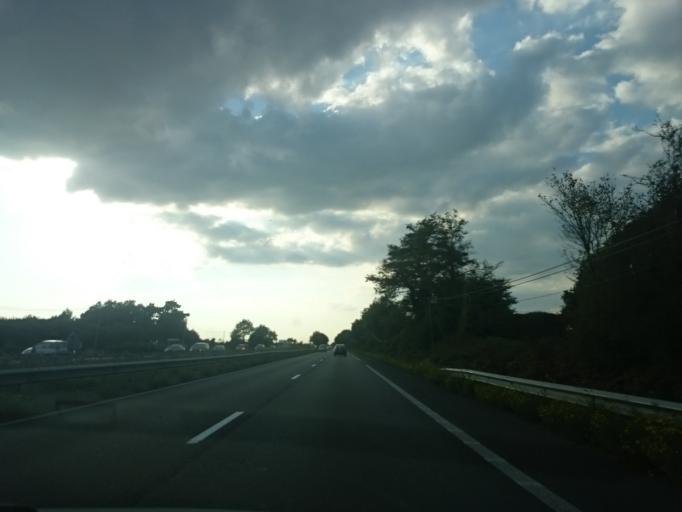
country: FR
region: Pays de la Loire
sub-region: Departement de la Loire-Atlantique
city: Le Temple-de-Bretagne
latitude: 47.3386
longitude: -1.8145
